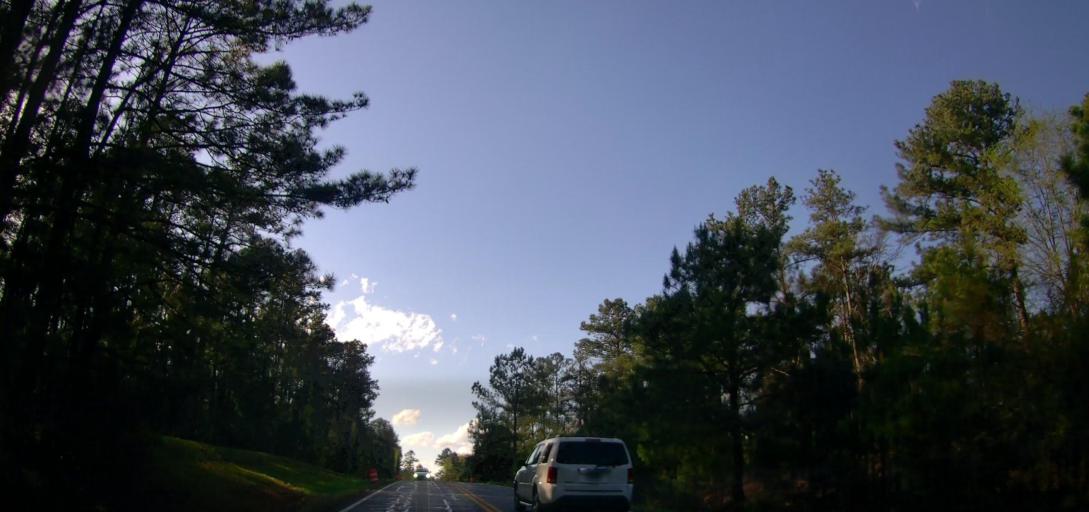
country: US
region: Georgia
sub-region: Baldwin County
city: Milledgeville
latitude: 33.1225
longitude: -83.2936
